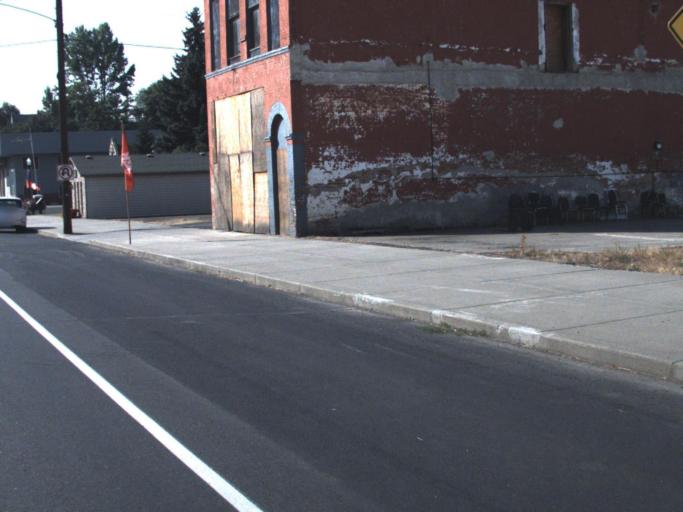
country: US
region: Washington
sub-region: Whitman County
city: Colfax
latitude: 47.1292
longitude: -117.2426
